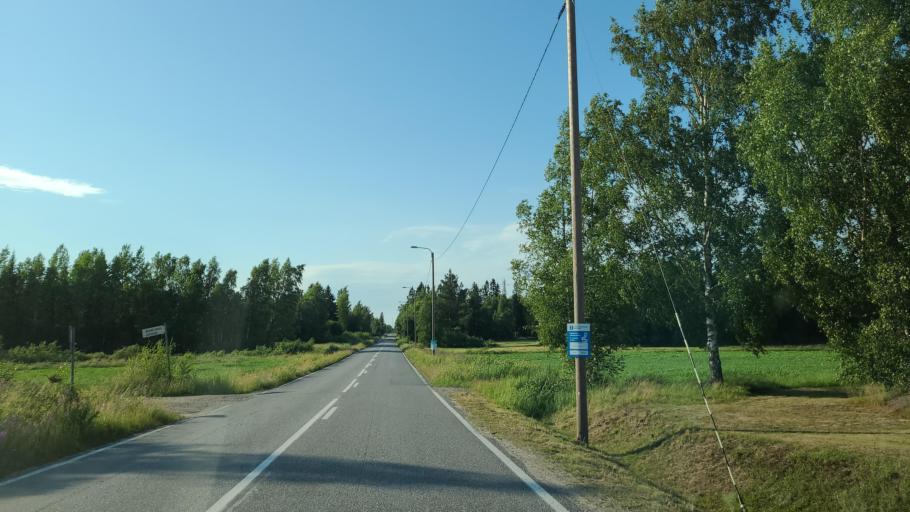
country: FI
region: Ostrobothnia
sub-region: Vaasa
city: Replot
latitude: 63.3245
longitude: 21.3436
